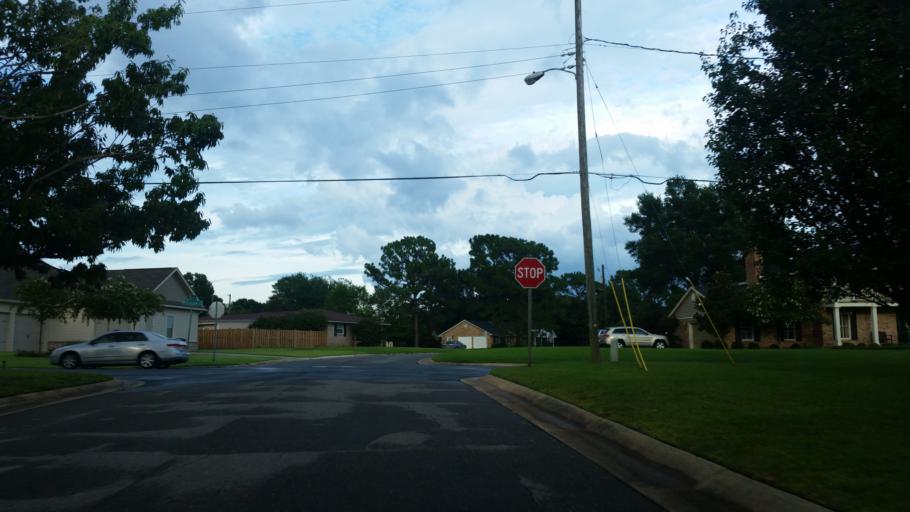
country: US
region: Florida
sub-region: Escambia County
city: Goulding
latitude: 30.4599
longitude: -87.1956
